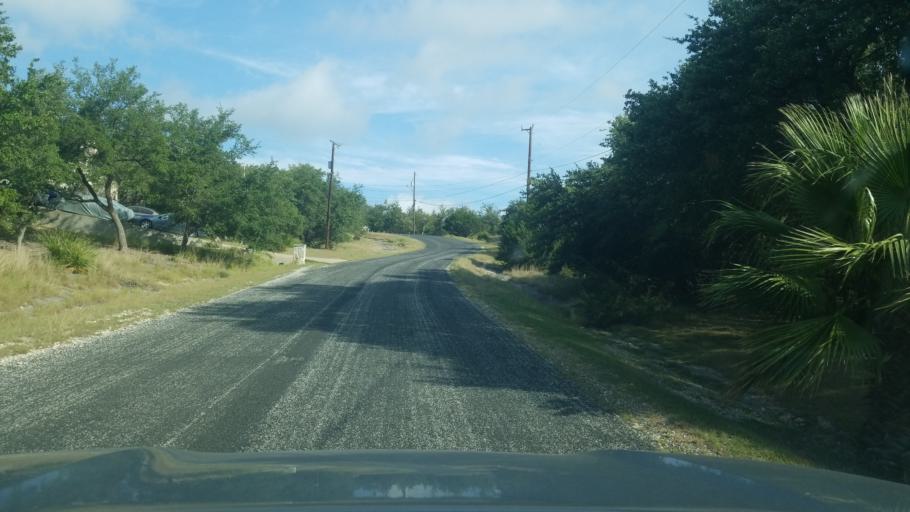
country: US
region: Texas
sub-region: Bexar County
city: Timberwood Park
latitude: 29.6848
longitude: -98.5044
